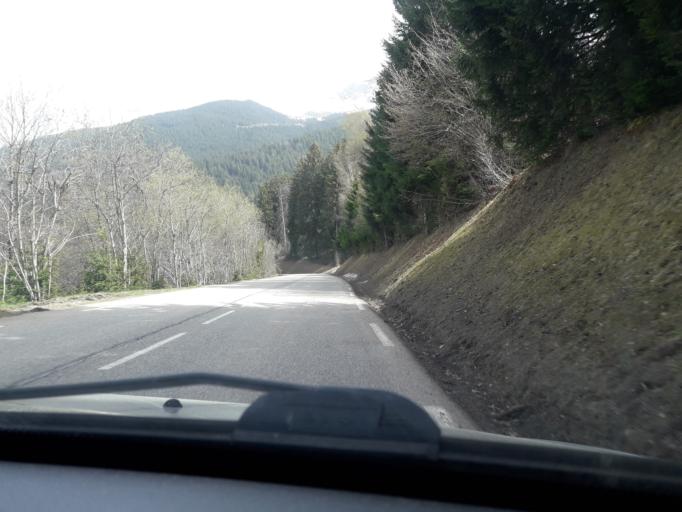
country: FR
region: Rhone-Alpes
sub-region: Departement de l'Isere
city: Theys
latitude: 45.2591
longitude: 5.9916
